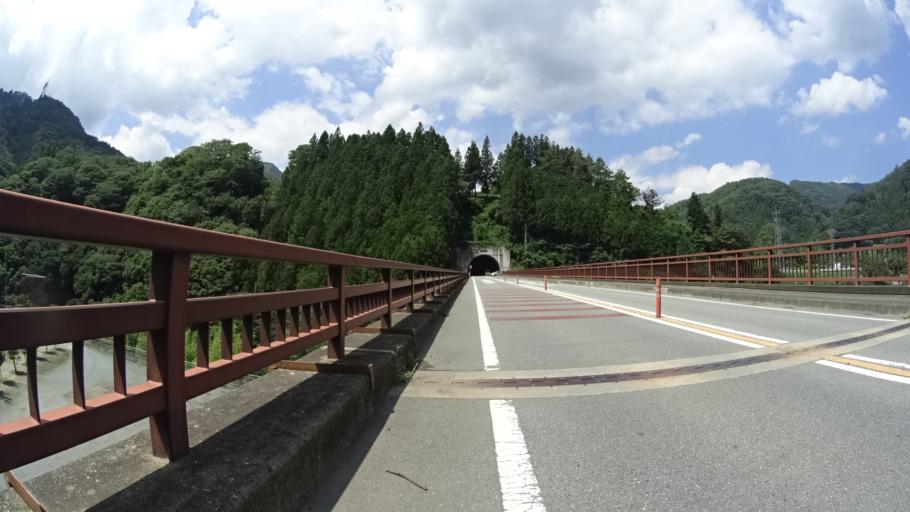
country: JP
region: Gunma
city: Tomioka
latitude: 36.0831
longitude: 138.7620
